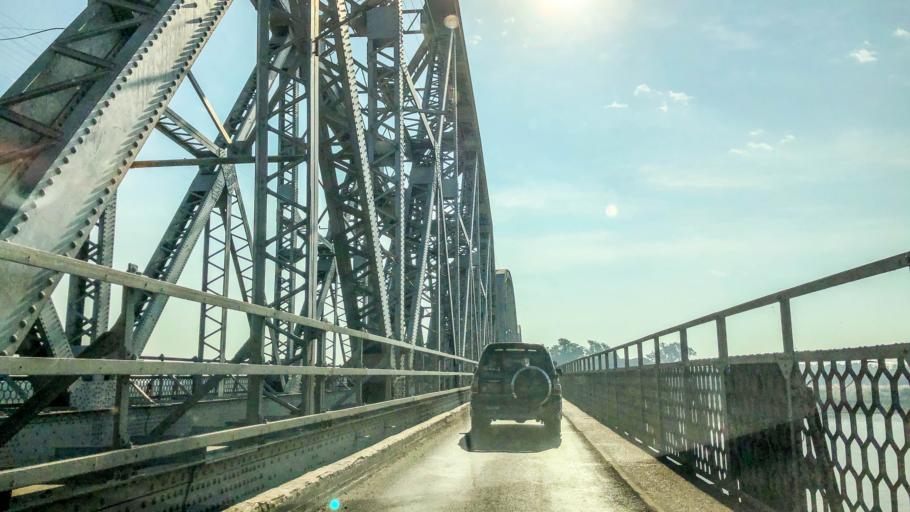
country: MM
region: Sagain
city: Sagaing
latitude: 21.8716
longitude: 95.9922
